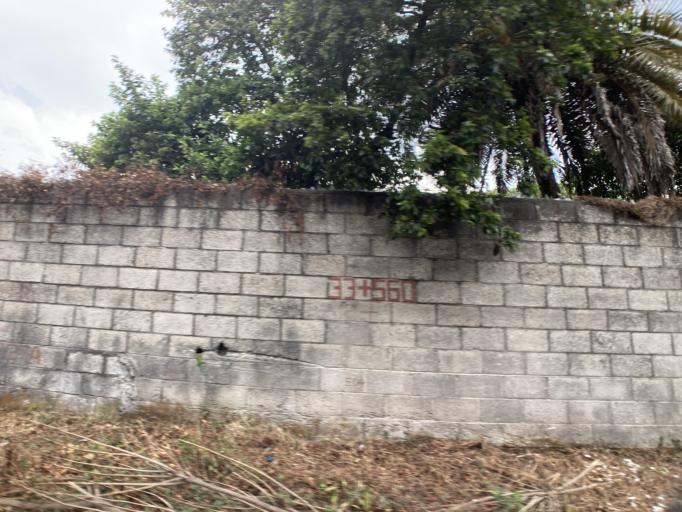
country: GT
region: Guatemala
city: Villa Canales
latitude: 14.4234
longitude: -90.5236
